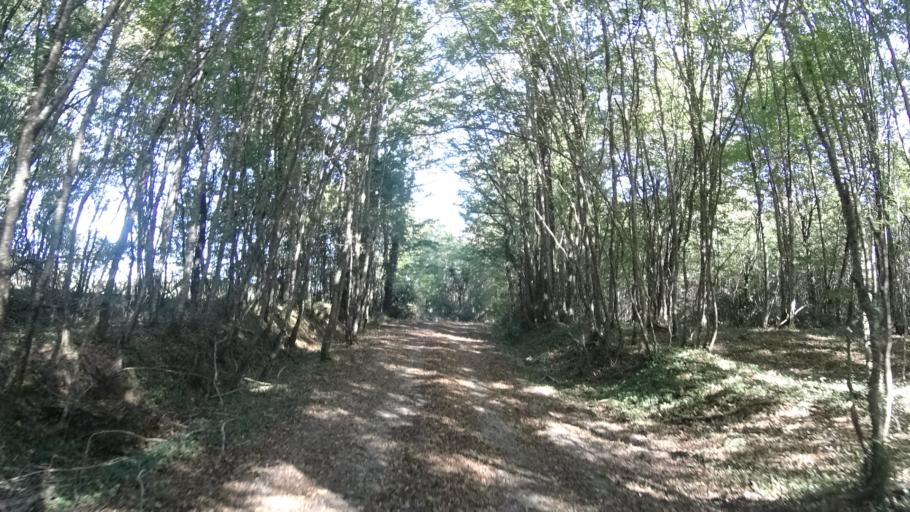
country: FR
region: Aquitaine
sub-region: Departement de la Dordogne
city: La Roche-Chalais
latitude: 45.1163
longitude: 0.0521
